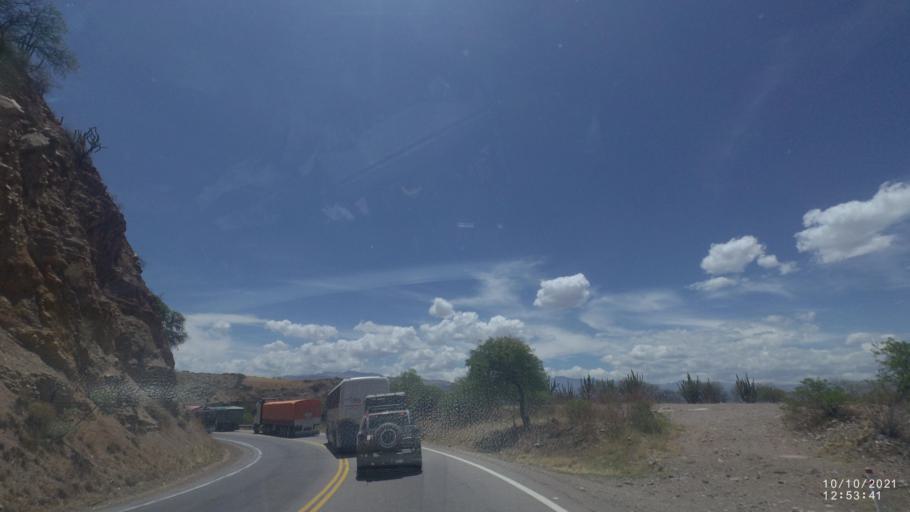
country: BO
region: Cochabamba
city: Capinota
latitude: -17.6121
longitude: -66.3563
